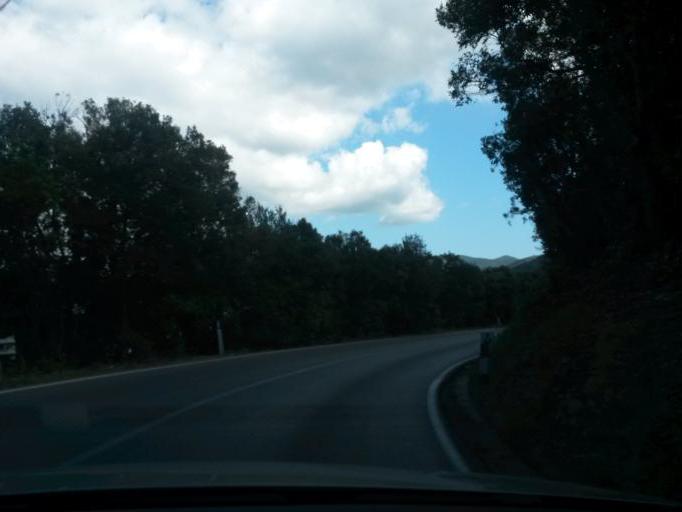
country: IT
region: Tuscany
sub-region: Provincia di Livorno
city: Marciana Marina
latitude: 42.7974
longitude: 10.2140
